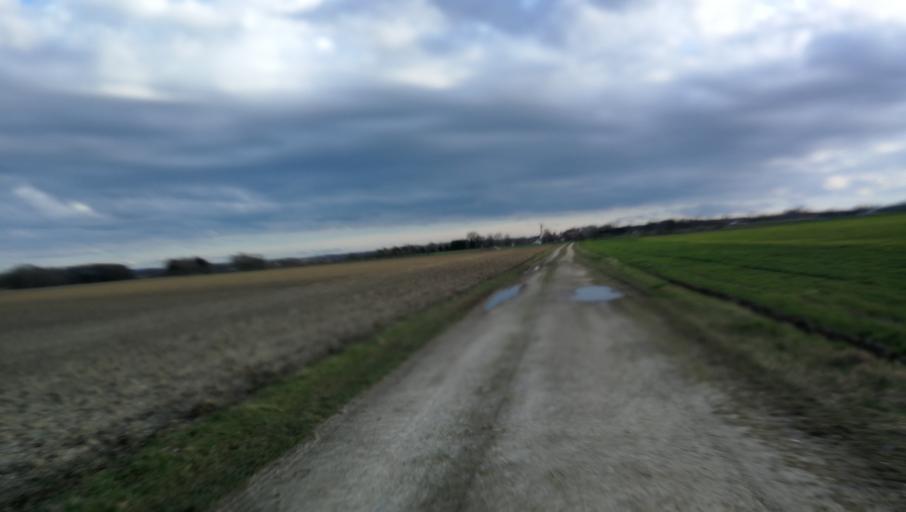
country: DE
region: Bavaria
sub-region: Upper Bavaria
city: Fuerstenfeldbruck
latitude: 48.2033
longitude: 11.2156
